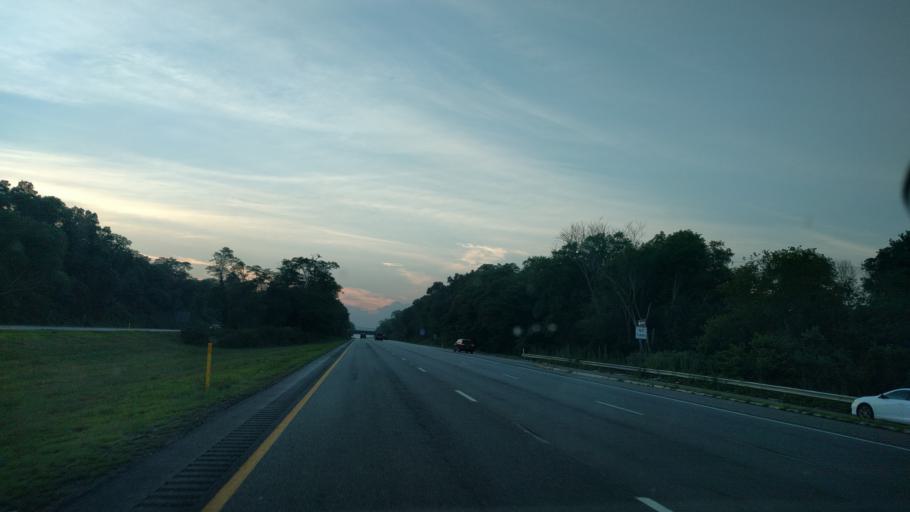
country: US
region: Massachusetts
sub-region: Bristol County
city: Ocean Grove
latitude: 41.7520
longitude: -71.2205
